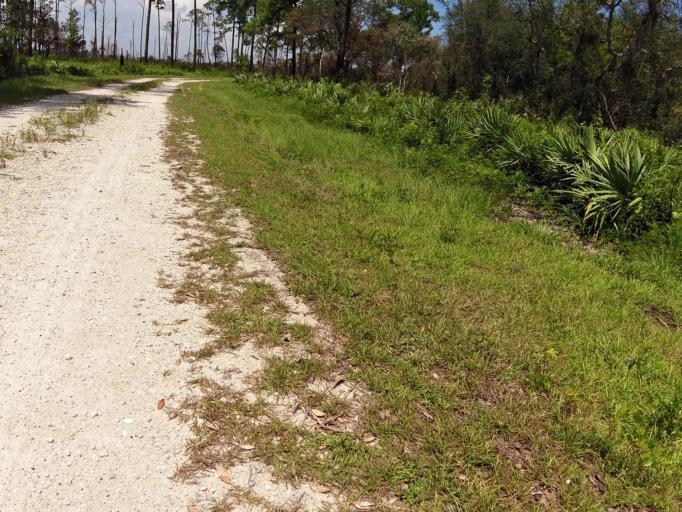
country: US
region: Florida
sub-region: Saint Johns County
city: Villano Beach
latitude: 30.0388
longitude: -81.3446
